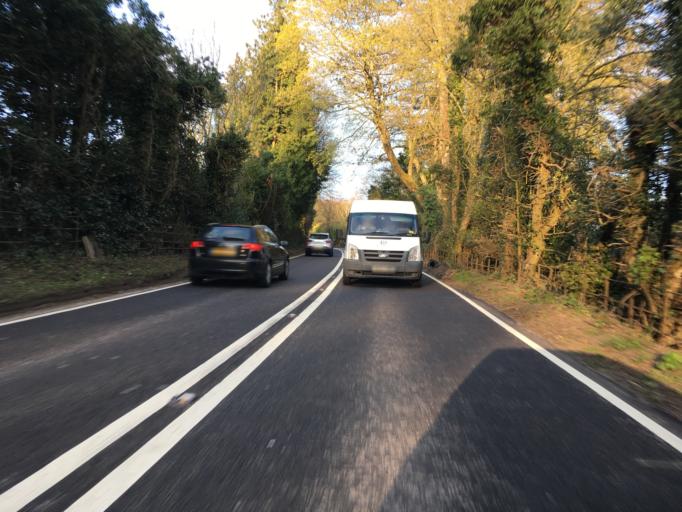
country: GB
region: England
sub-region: Gloucestershire
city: Shurdington
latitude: 51.8470
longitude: -2.0809
